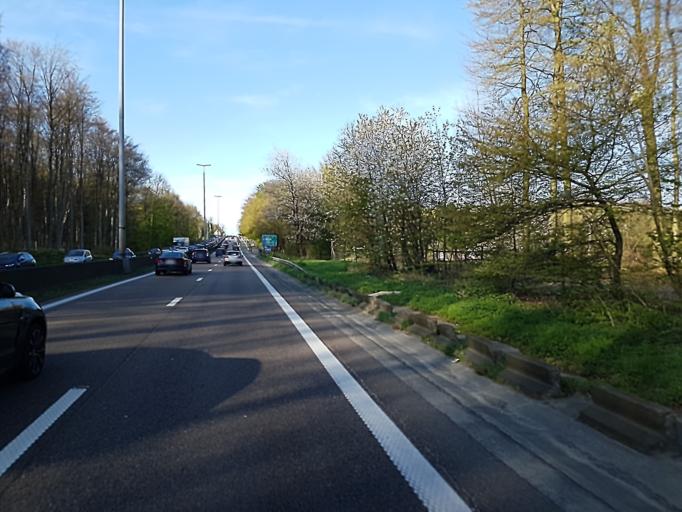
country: BE
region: Flanders
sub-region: Provincie Vlaams-Brabant
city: Hoeilaart
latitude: 50.7771
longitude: 4.4498
